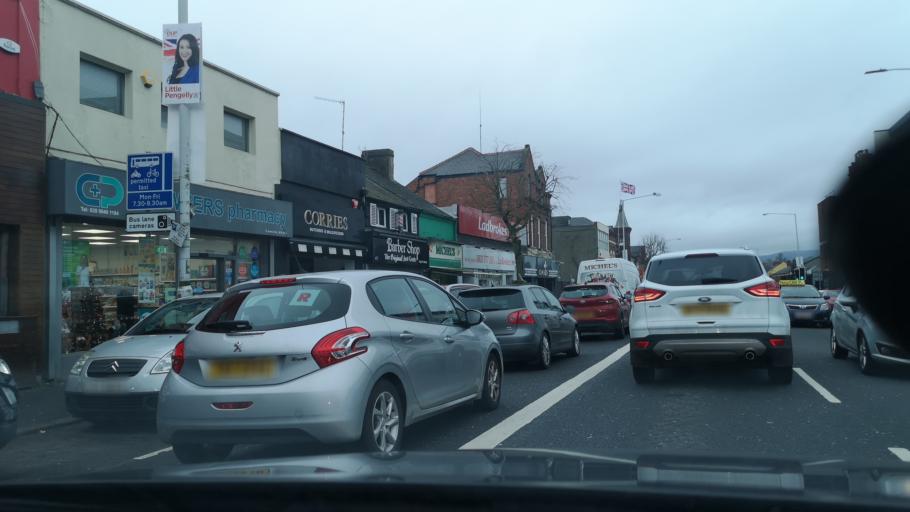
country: GB
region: Northern Ireland
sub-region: City of Belfast
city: Belfast
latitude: 54.5761
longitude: -5.9182
